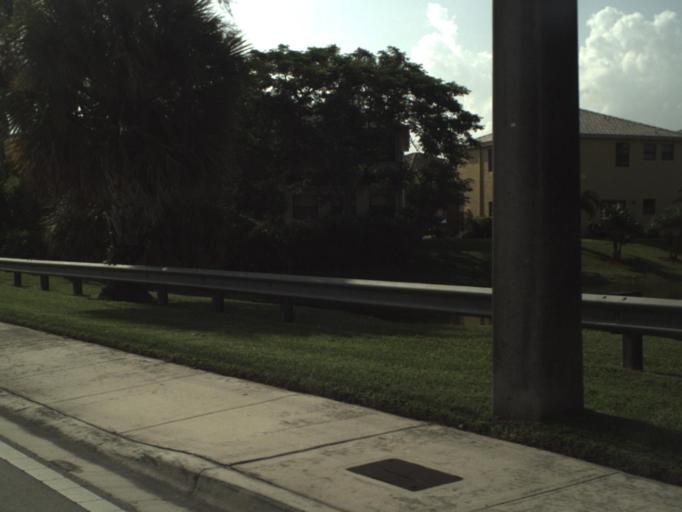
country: US
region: Florida
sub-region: Broward County
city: Coral Springs
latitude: 26.2728
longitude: -80.2741
